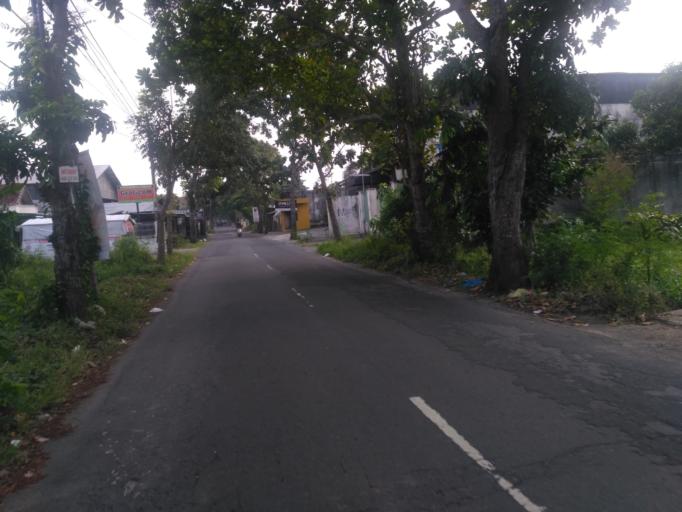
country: ID
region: Daerah Istimewa Yogyakarta
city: Yogyakarta
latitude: -7.7751
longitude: 110.3421
